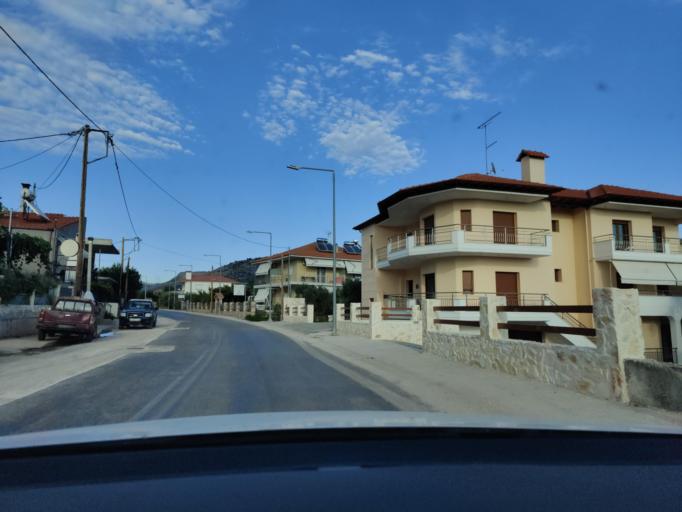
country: GR
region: East Macedonia and Thrace
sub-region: Nomos Kavalas
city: Limenaria
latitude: 40.6116
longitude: 24.6159
